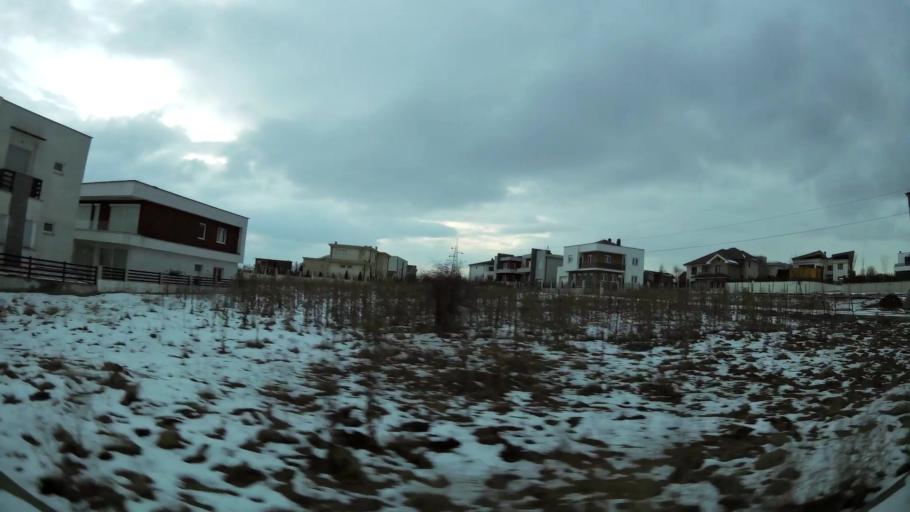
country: XK
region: Pristina
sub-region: Komuna e Prishtines
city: Pristina
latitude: 42.6183
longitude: 21.1672
